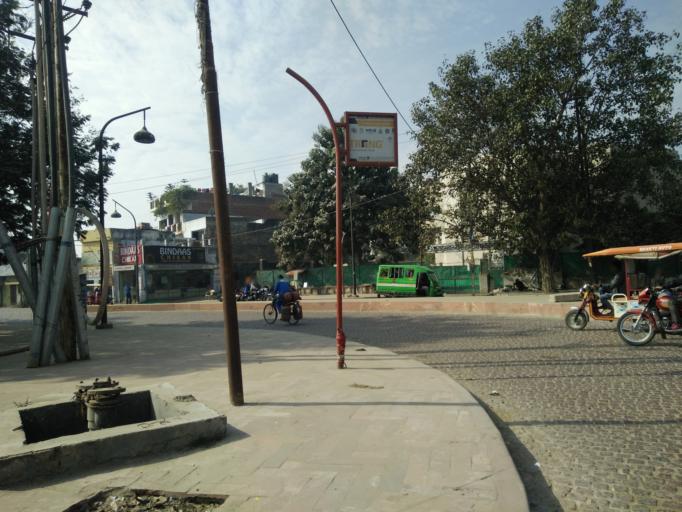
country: IN
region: Uttar Pradesh
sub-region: Lucknow District
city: Lucknow
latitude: 26.8718
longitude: 80.9109
